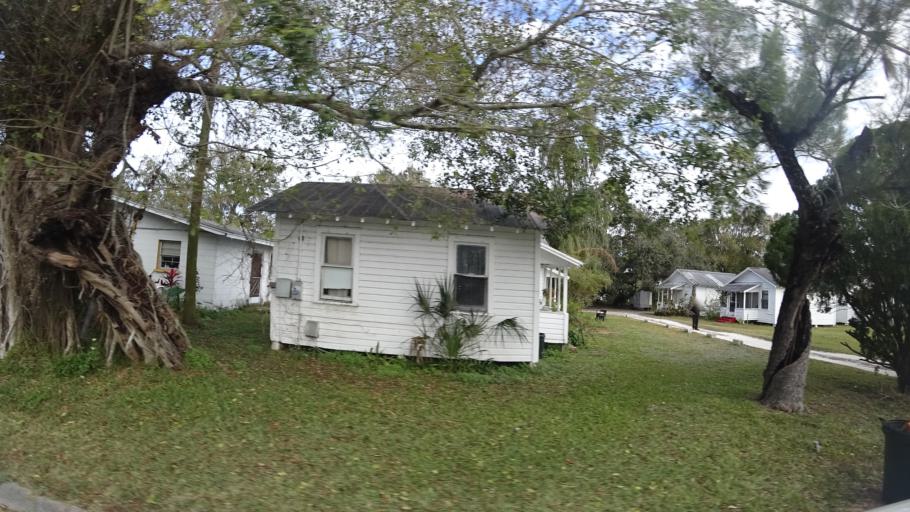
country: US
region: Florida
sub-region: Manatee County
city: West Samoset
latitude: 27.4734
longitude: -82.5537
